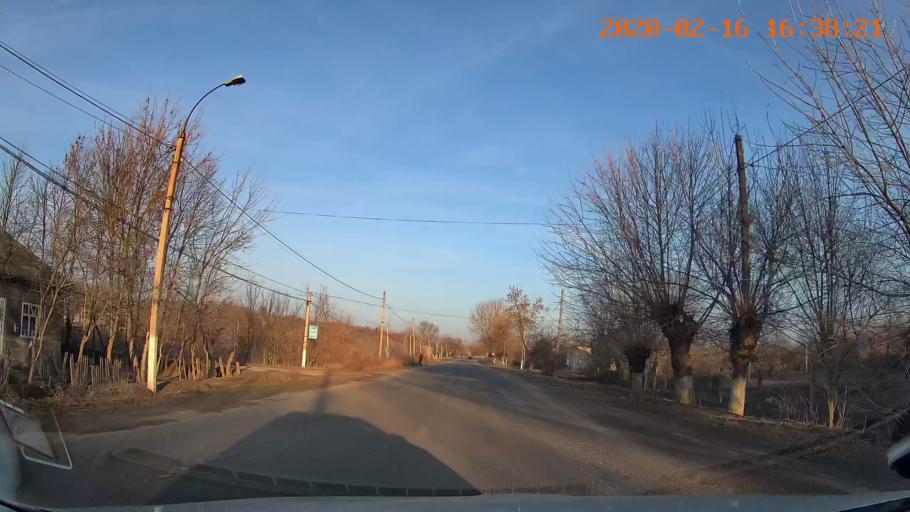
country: RO
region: Botosani
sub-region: Comuna Radauti-Prut
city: Rediu
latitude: 48.2697
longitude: 26.7231
